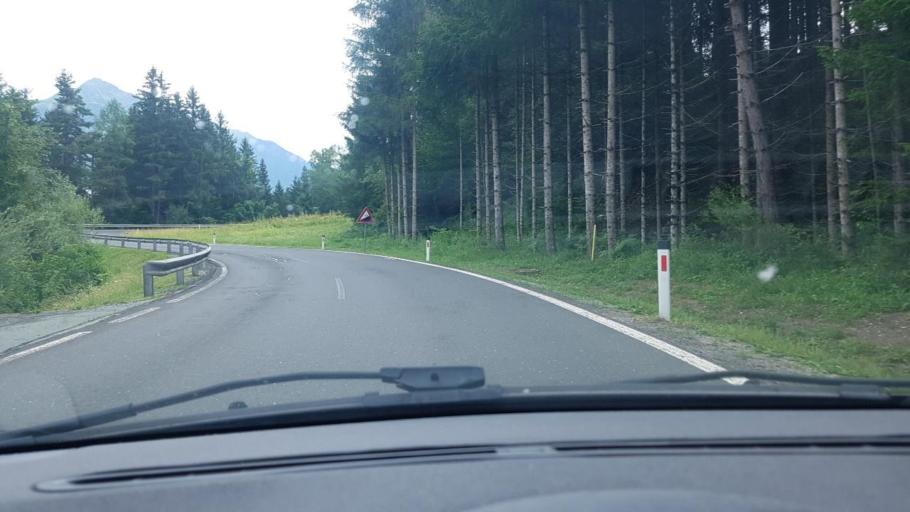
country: AT
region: Carinthia
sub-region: Politischer Bezirk Spittal an der Drau
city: Greifenburg
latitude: 46.7362
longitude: 13.2189
